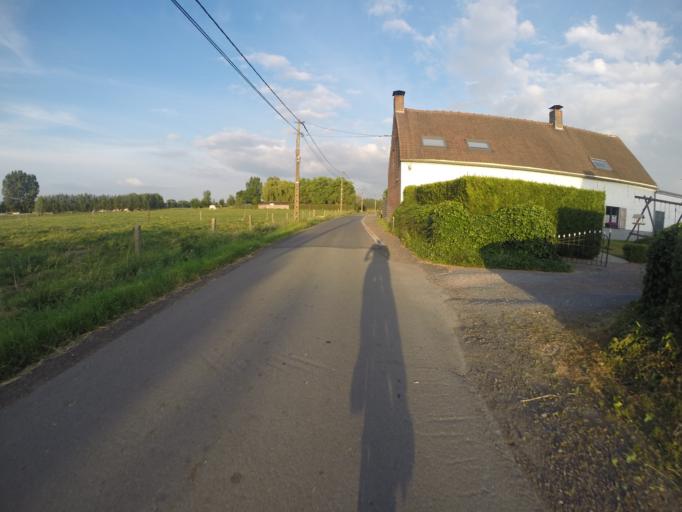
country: BE
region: Flanders
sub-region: Provincie West-Vlaanderen
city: Beernem
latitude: 51.1497
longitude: 3.3058
